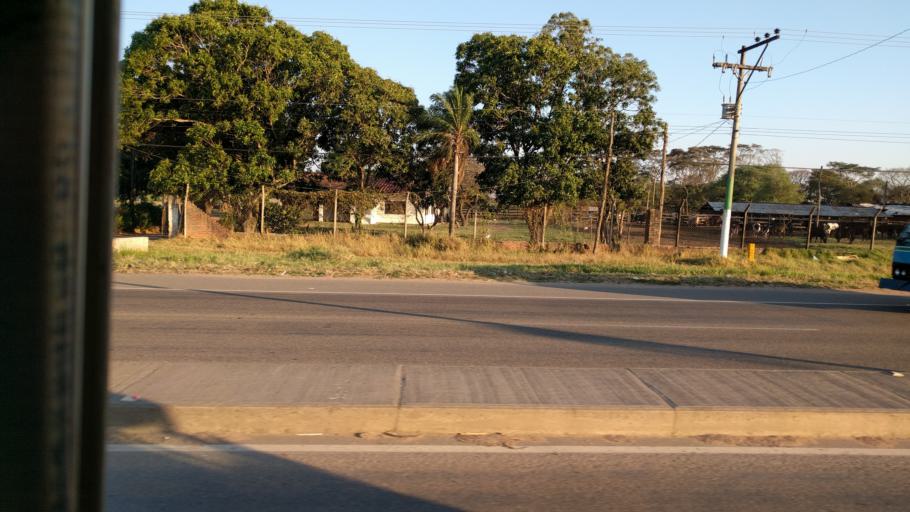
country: BO
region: Santa Cruz
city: Cotoca
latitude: -17.7621
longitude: -63.0249
